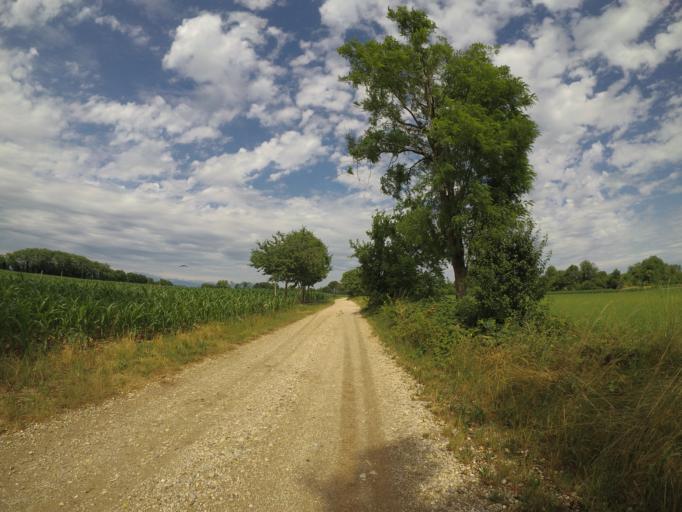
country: IT
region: Friuli Venezia Giulia
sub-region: Provincia di Udine
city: Lestizza
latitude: 45.9654
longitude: 13.1246
